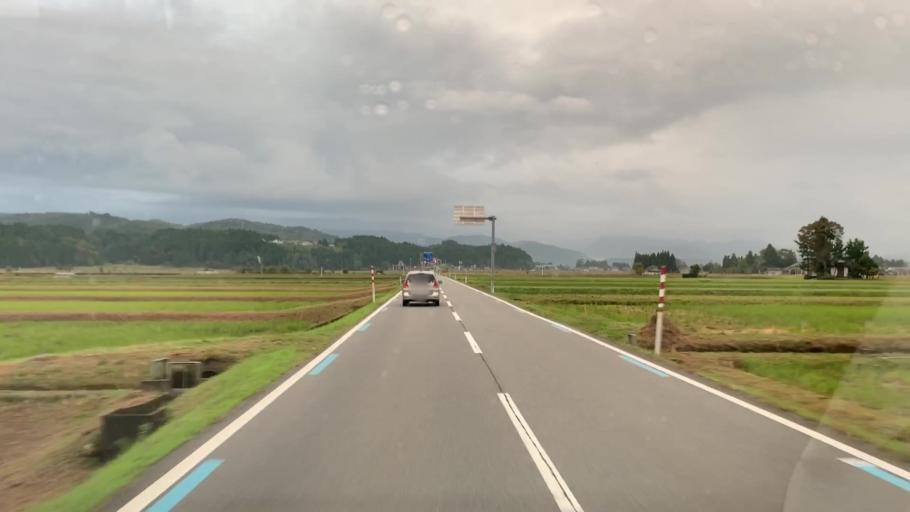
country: JP
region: Toyama
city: Kamiichi
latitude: 36.6290
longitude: 137.3286
